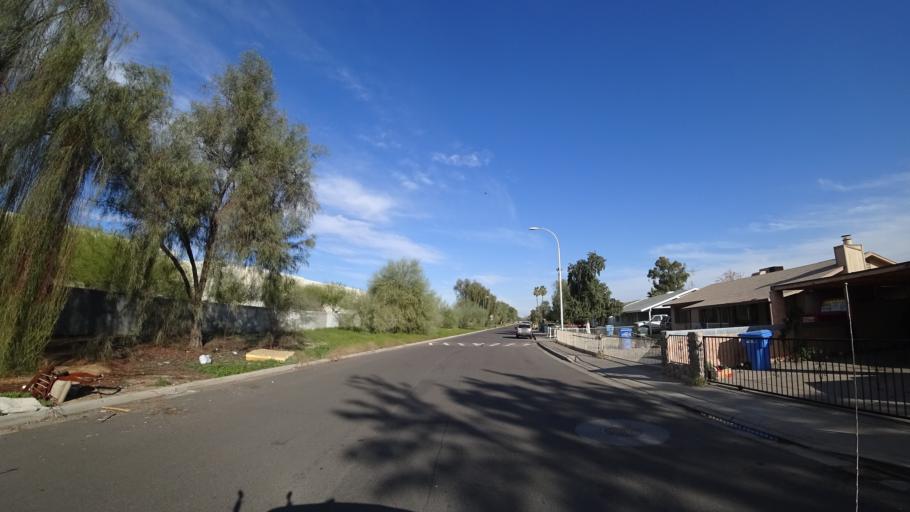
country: US
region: Arizona
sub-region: Maricopa County
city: Tolleson
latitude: 33.4586
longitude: -112.2099
